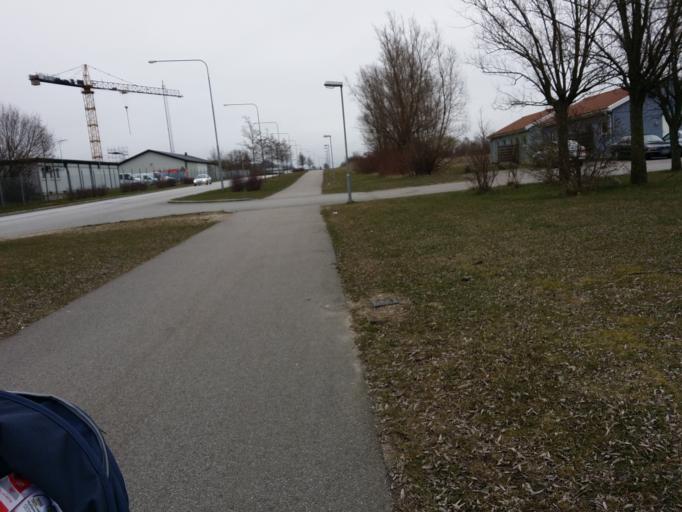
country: SE
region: Skane
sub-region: Burlovs Kommun
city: Arloev
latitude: 55.6103
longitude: 13.0848
